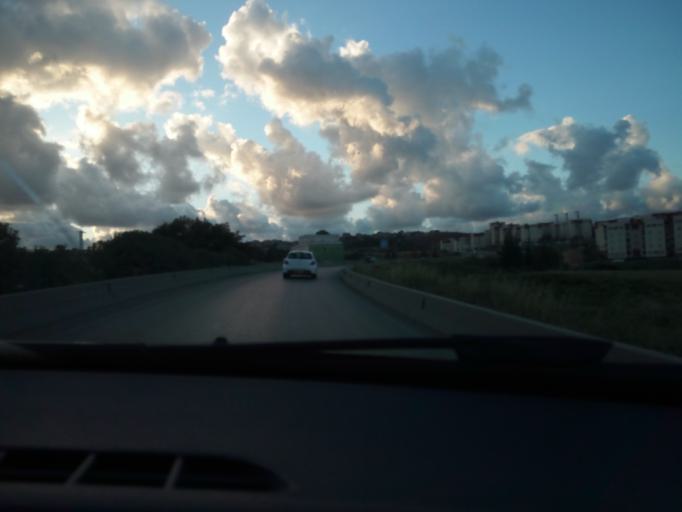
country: DZ
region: Tipaza
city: Saoula
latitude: 36.6531
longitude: 3.0120
